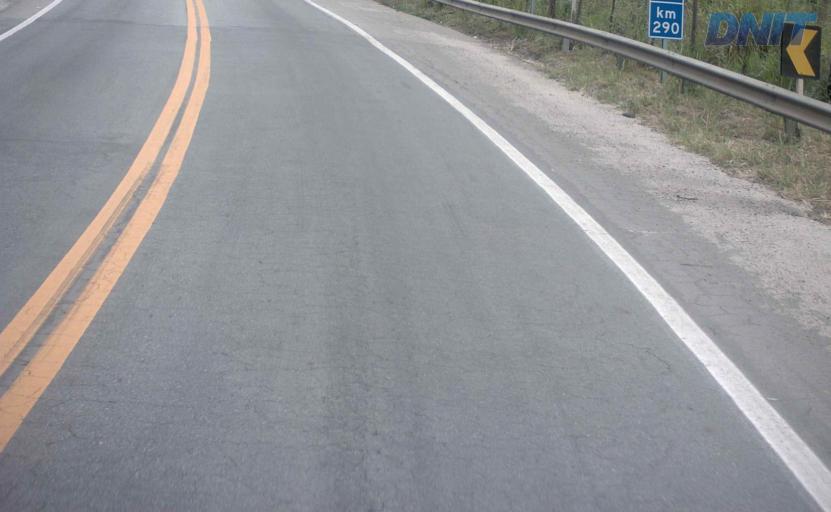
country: BR
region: Minas Gerais
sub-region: Timoteo
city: Timoteo
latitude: -19.6160
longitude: -42.7929
